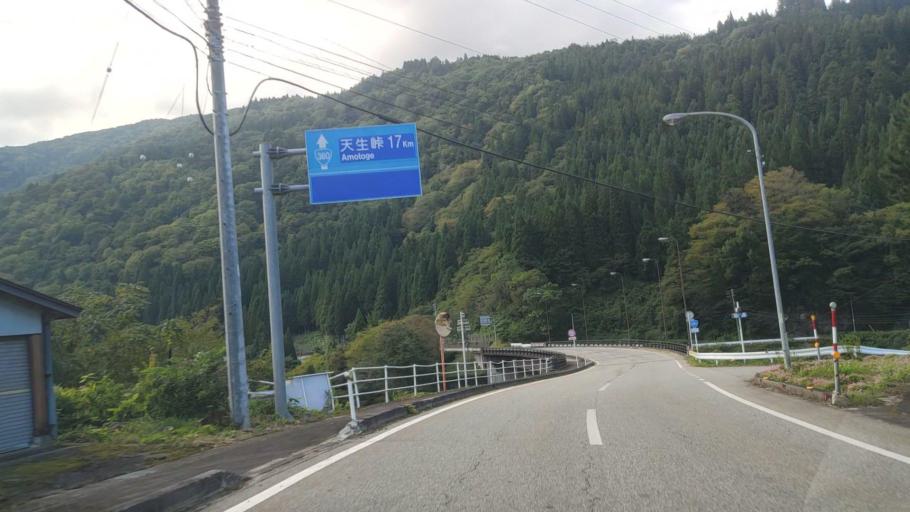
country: JP
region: Gifu
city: Takayama
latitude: 36.3060
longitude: 137.0924
